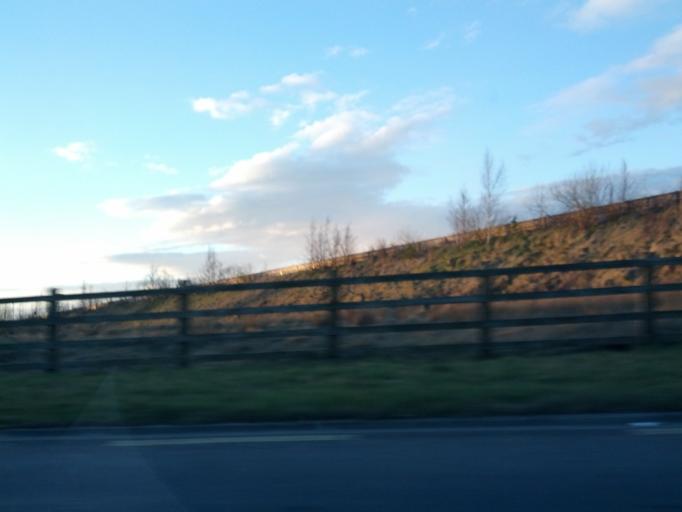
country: IE
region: Connaught
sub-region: County Galway
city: Athenry
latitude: 53.2710
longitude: -8.6768
